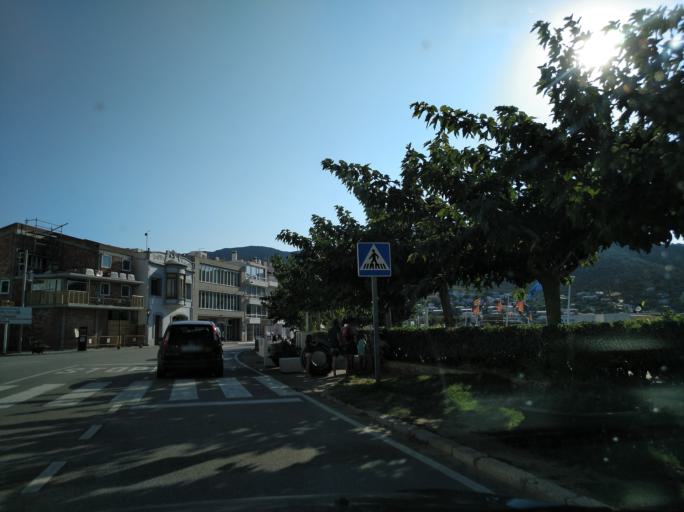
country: ES
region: Catalonia
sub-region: Provincia de Girona
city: Llanca
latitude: 42.3359
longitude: 3.2029
